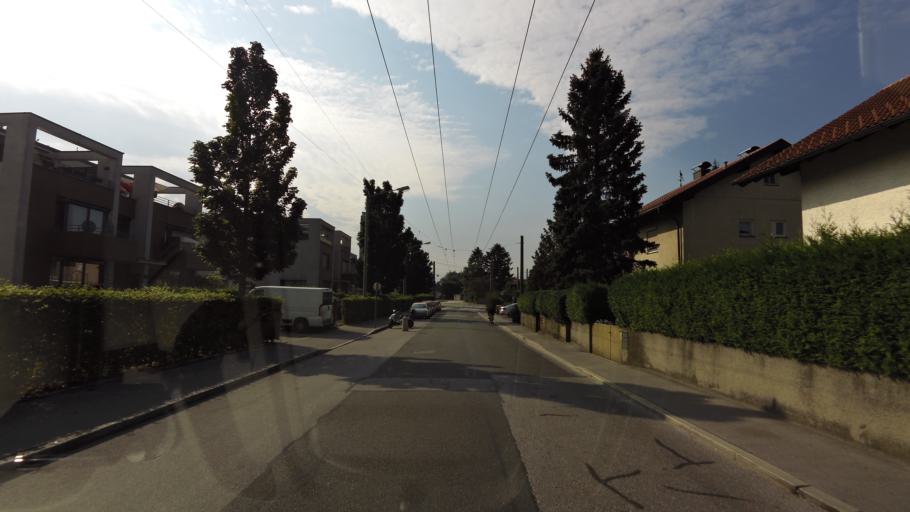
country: AT
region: Salzburg
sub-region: Politischer Bezirk Salzburg-Umgebung
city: Bergheim
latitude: 47.8298
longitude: 13.0223
